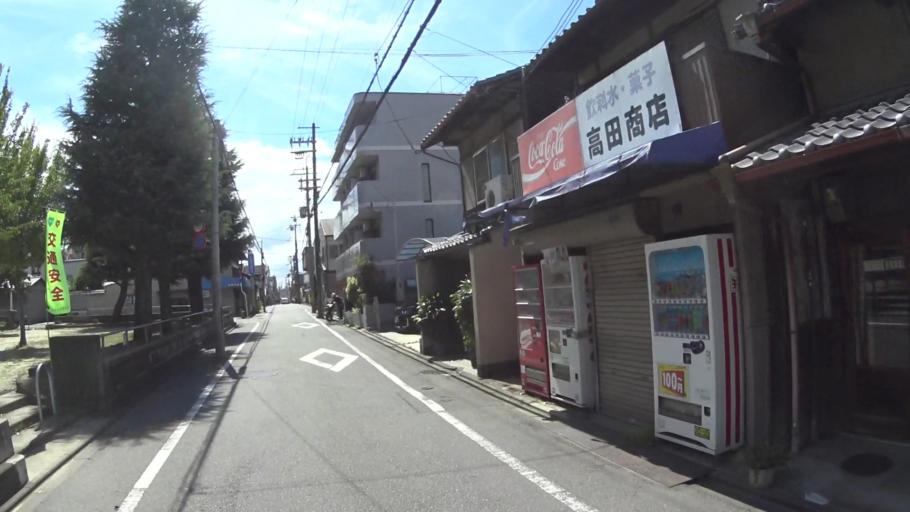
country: JP
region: Kyoto
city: Muko
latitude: 34.9503
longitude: 135.7671
